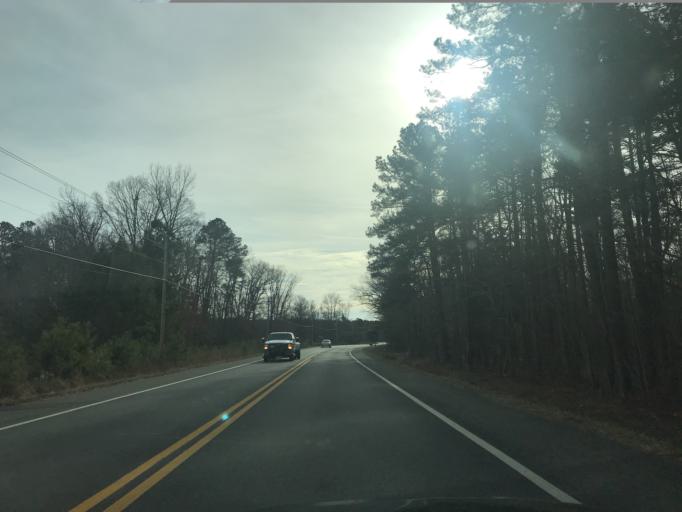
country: US
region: Maryland
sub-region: Charles County
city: Cobb Island
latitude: 38.2908
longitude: -76.8782
